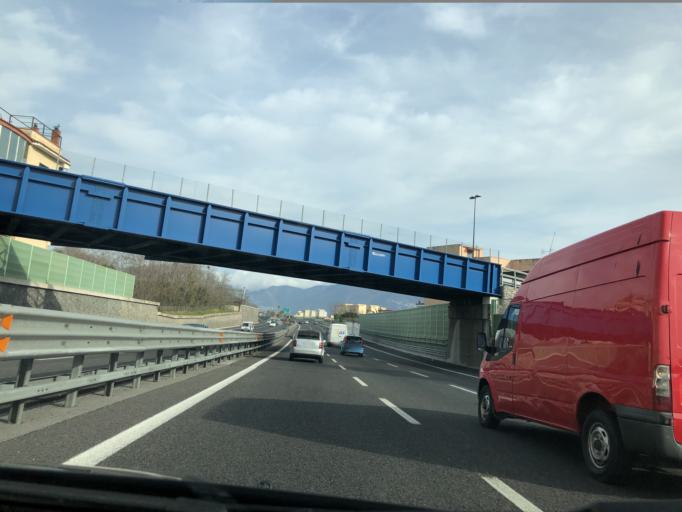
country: IT
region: Campania
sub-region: Provincia di Napoli
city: Trecase
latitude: 40.7631
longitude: 14.4397
